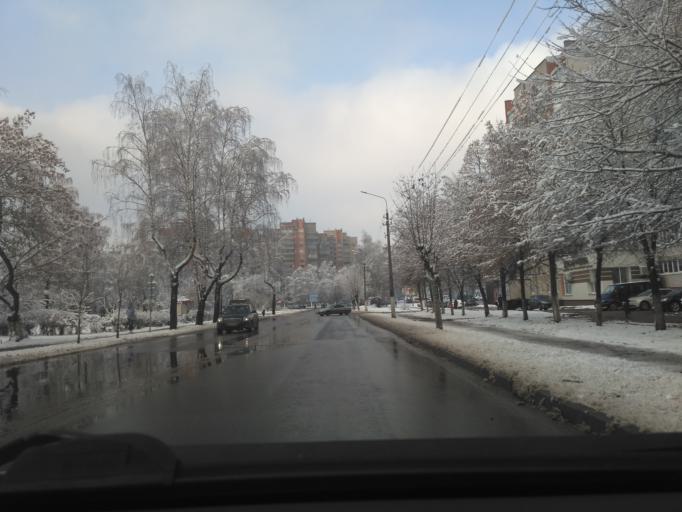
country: BY
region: Minsk
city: Horad Barysaw
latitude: 54.2188
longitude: 28.4945
